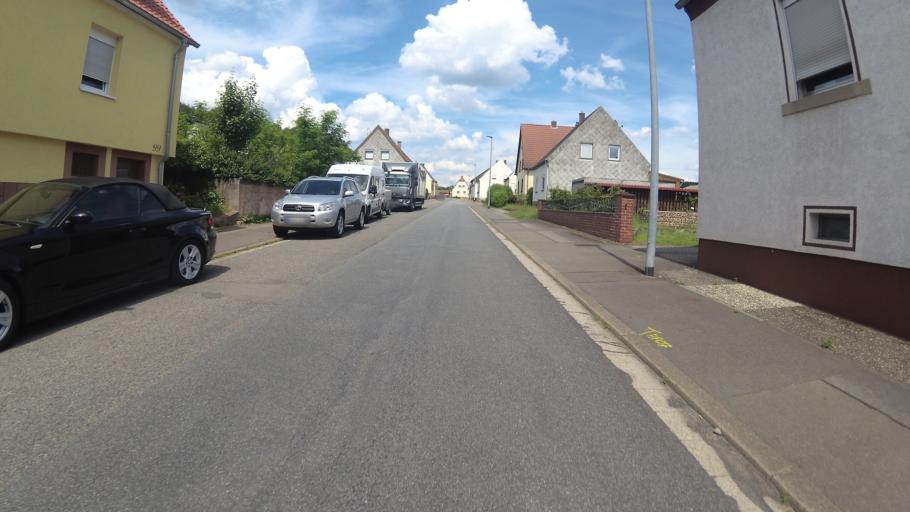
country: DE
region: Saarland
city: Homburg
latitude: 49.3073
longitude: 7.3714
